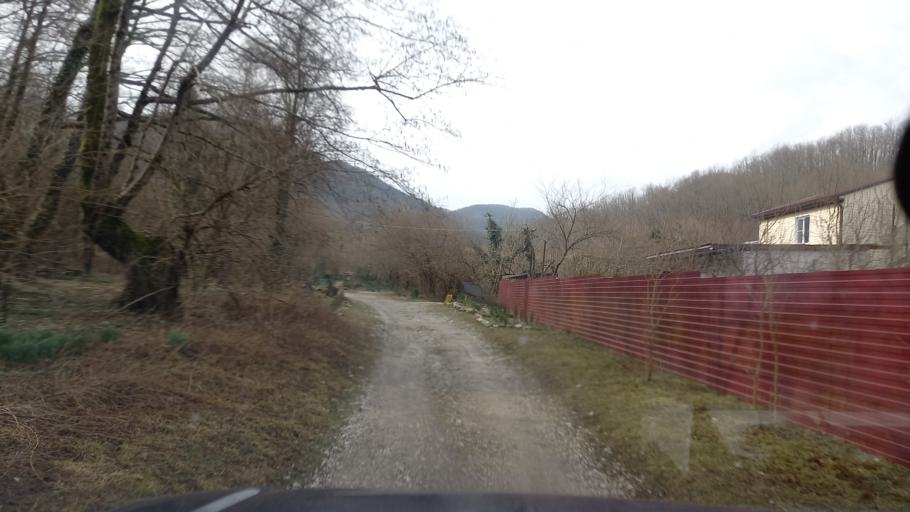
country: RU
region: Krasnodarskiy
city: Dzhubga
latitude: 44.4147
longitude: 38.7206
